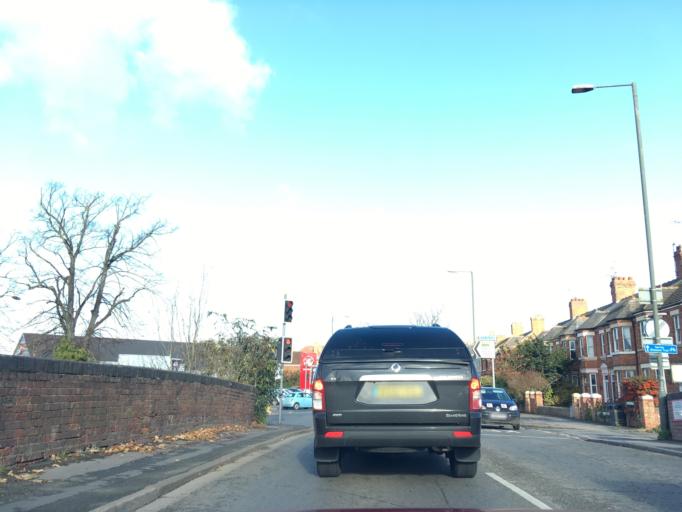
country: GB
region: England
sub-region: Worcestershire
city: Evesham
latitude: 52.0981
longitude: -1.9461
